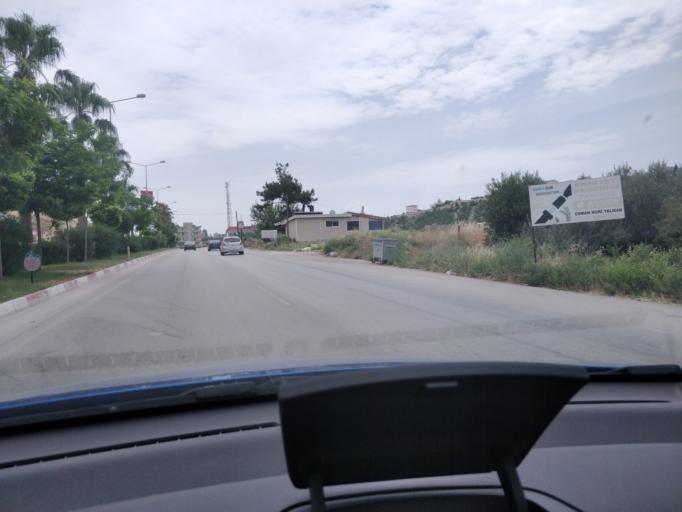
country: TR
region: Mersin
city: Mut
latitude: 36.6491
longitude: 33.4266
